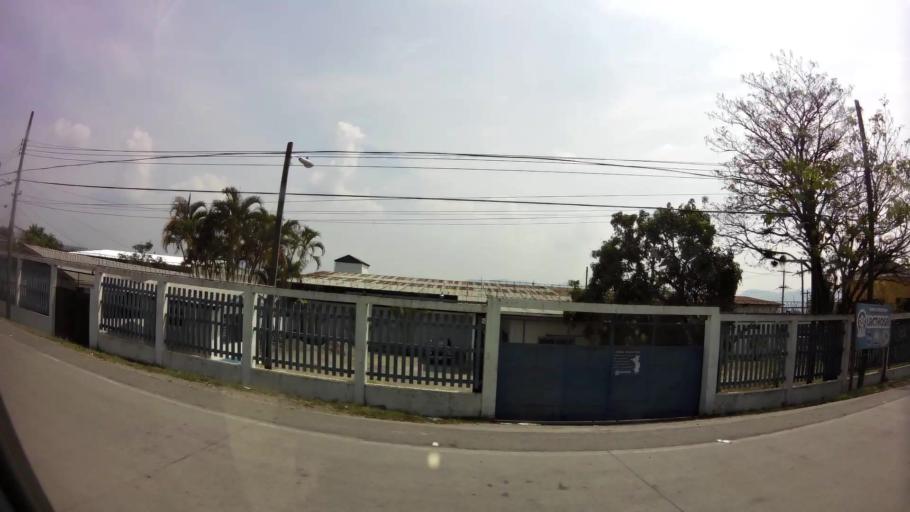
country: HN
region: Comayagua
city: Siguatepeque
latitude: 14.5853
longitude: -87.8495
